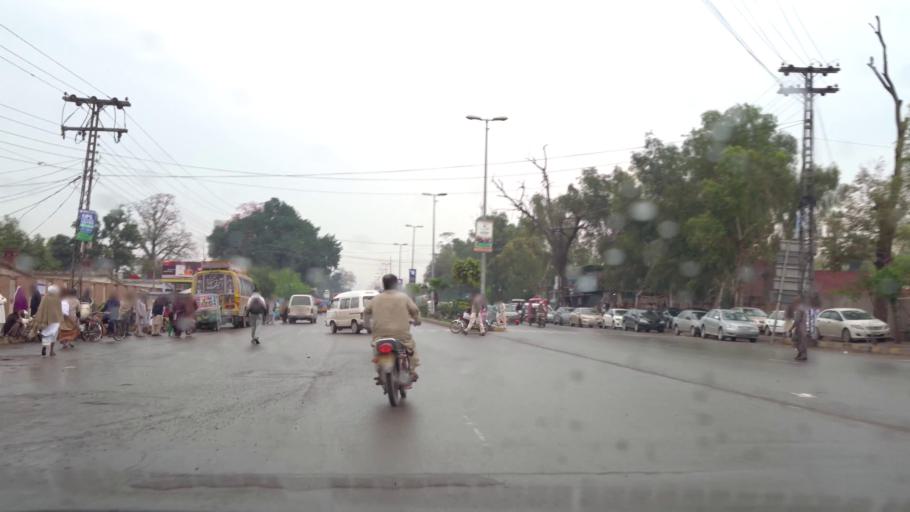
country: PK
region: Punjab
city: Faisalabad
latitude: 31.4204
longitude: 73.0868
